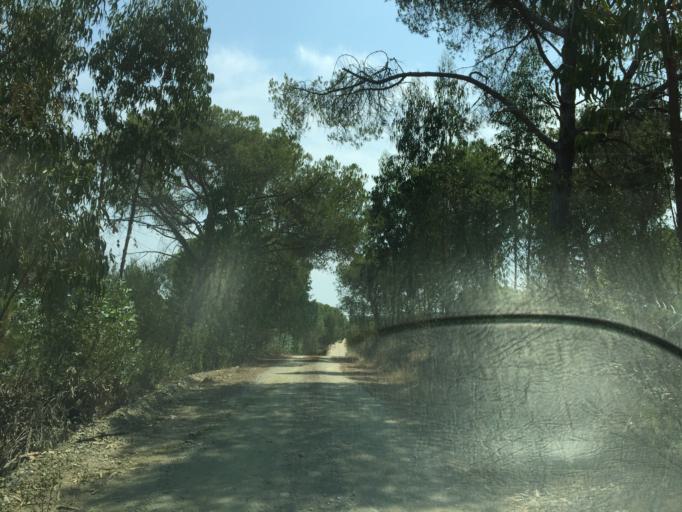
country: PT
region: Setubal
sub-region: Grandola
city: Grandola
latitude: 38.1077
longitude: -8.4909
